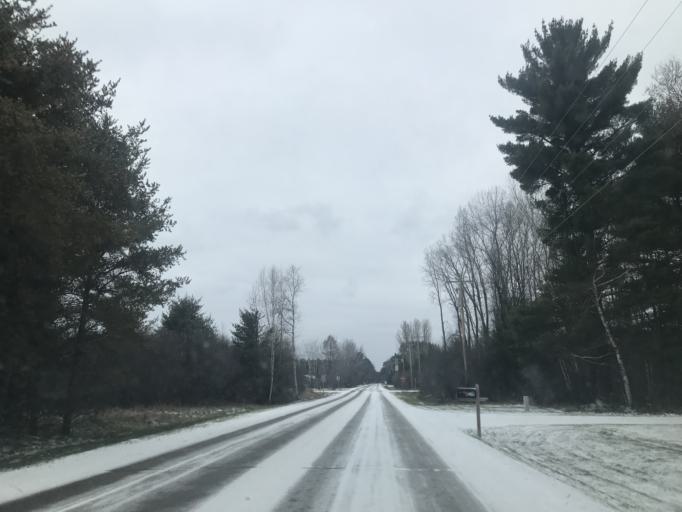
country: US
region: Wisconsin
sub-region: Marinette County
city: Marinette
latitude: 45.0558
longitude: -87.6582
